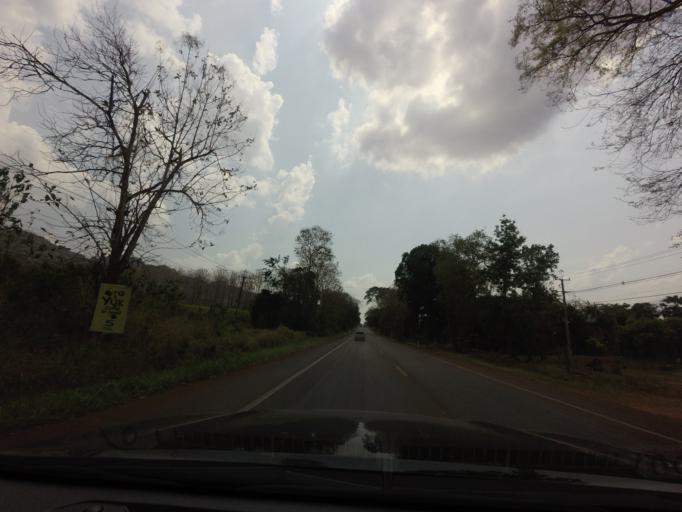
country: TH
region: Kanchanaburi
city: Sai Yok
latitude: 14.1593
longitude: 99.1378
